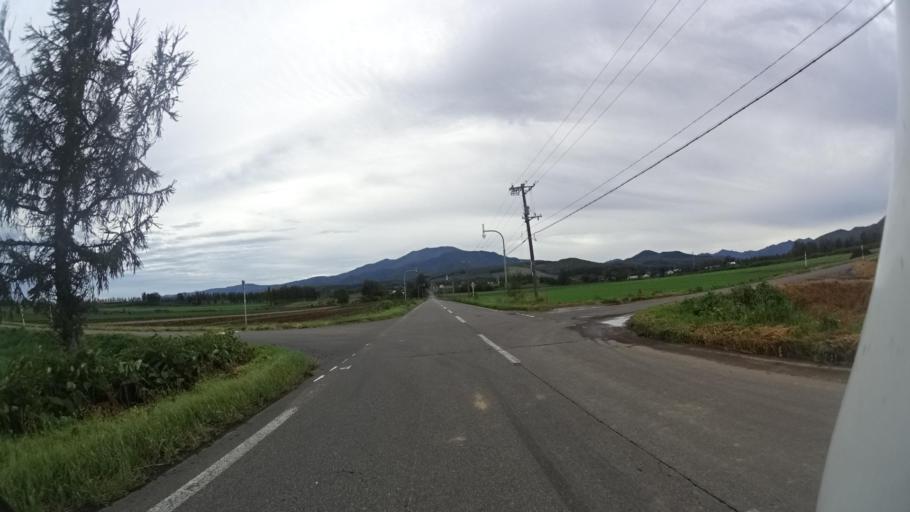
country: JP
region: Hokkaido
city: Shibetsu
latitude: 43.8741
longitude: 144.7389
